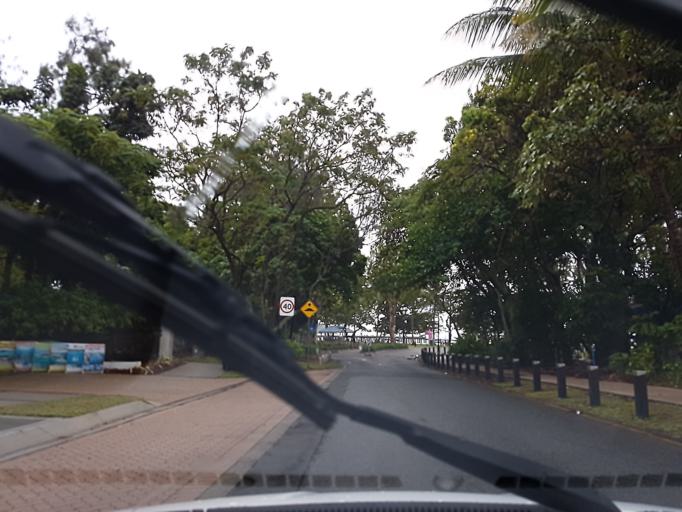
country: AU
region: Queensland
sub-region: Cairns
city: Palm Cove
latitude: -16.7417
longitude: 145.6705
